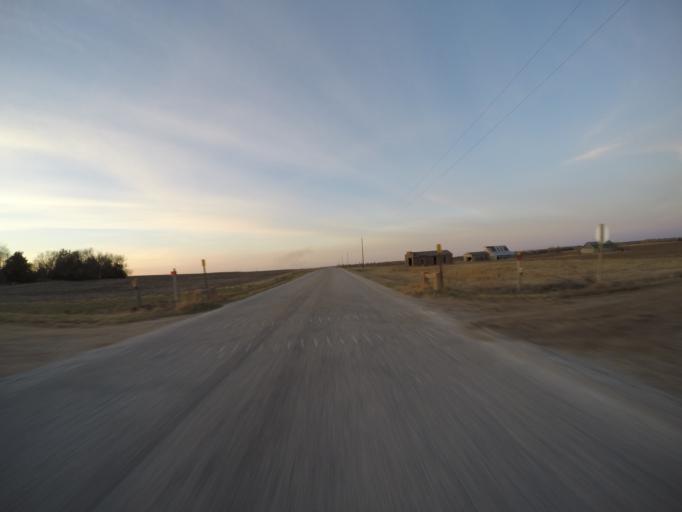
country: US
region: Kansas
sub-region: Washington County
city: Washington
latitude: 39.5956
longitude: -96.9943
